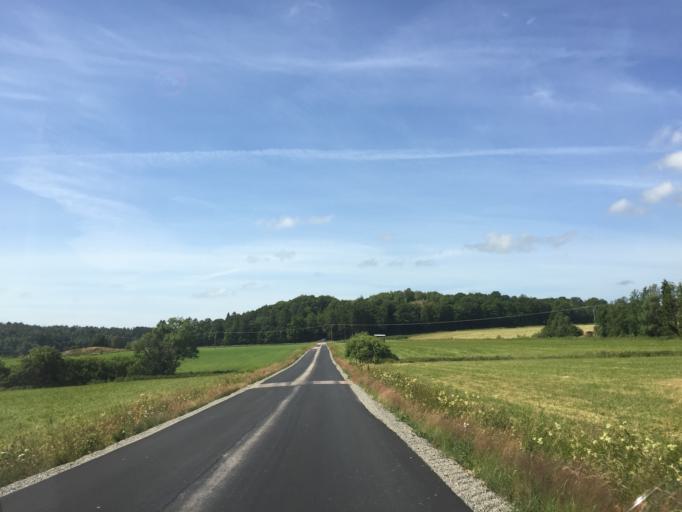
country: SE
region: Vaestra Goetaland
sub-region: Orust
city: Henan
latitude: 58.2816
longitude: 11.5985
